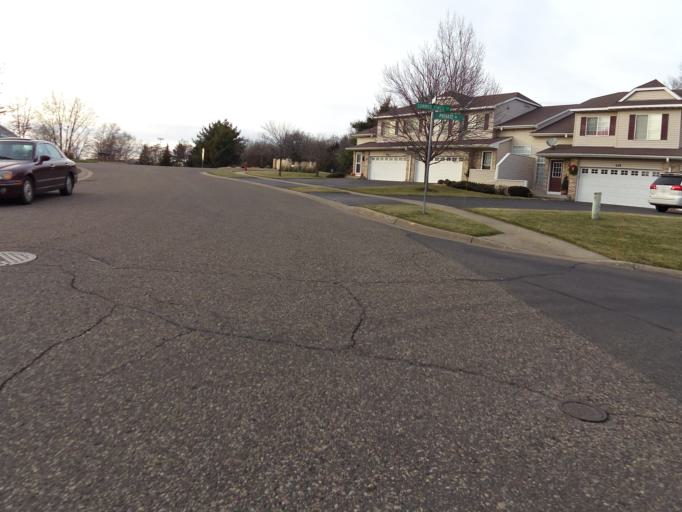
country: US
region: Wisconsin
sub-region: Saint Croix County
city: Hudson
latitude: 44.9772
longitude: -92.7328
